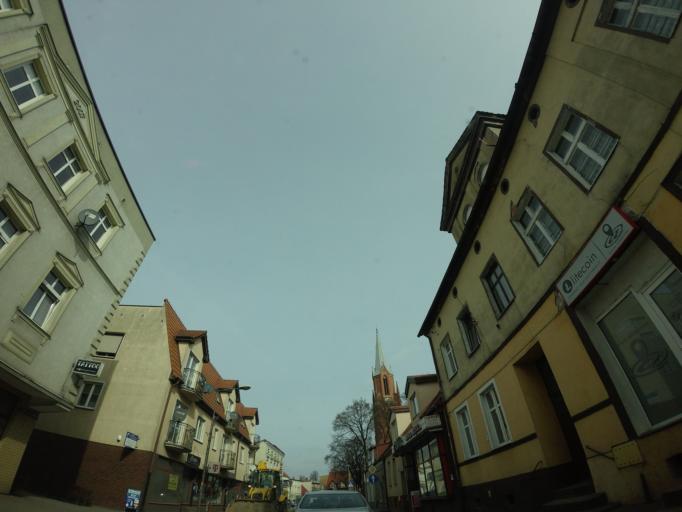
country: PL
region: West Pomeranian Voivodeship
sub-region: Powiat walecki
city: Walcz
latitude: 53.2701
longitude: 16.4658
